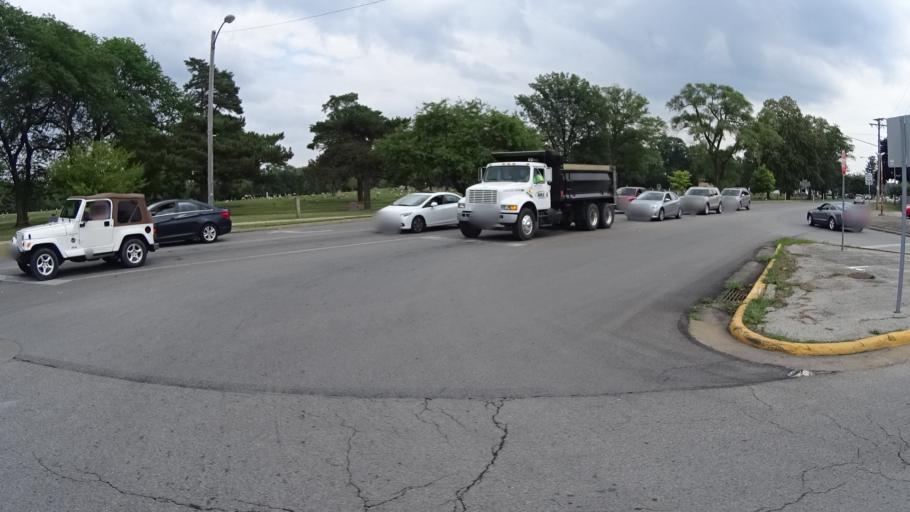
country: US
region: Ohio
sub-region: Erie County
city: Sandusky
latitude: 41.4396
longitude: -82.7347
